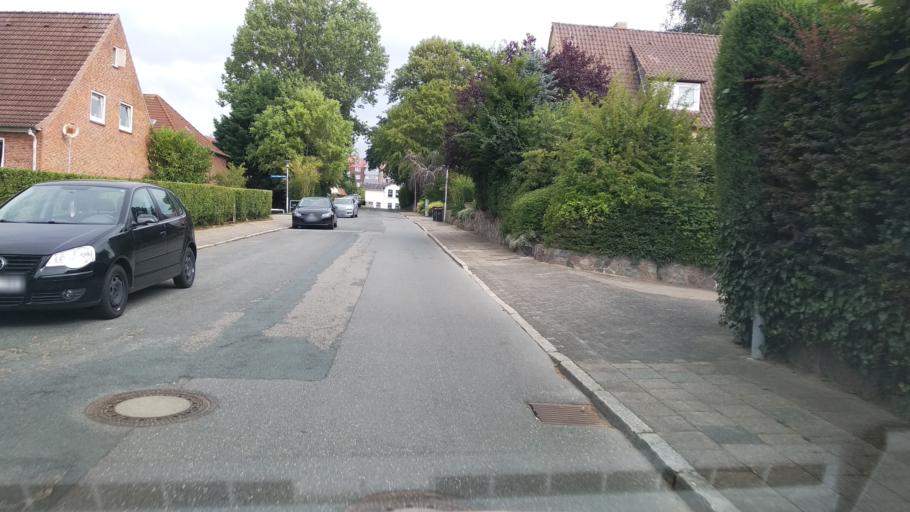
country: DE
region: Schleswig-Holstein
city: Schleswig
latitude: 54.5192
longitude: 9.5754
